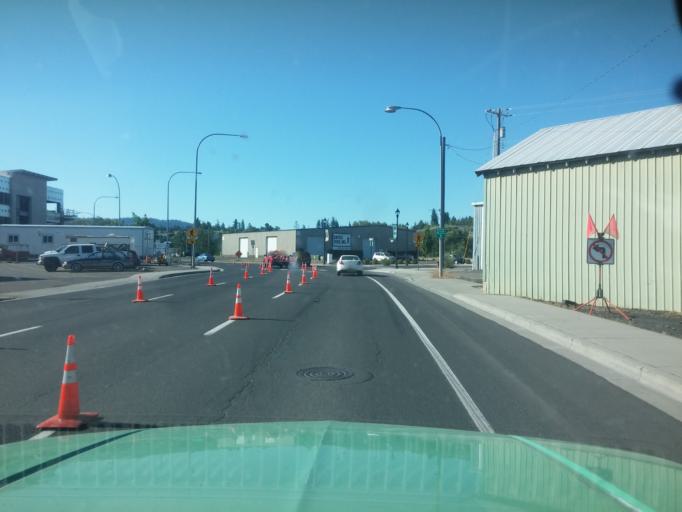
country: US
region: Idaho
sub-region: Latah County
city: Moscow
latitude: 46.7287
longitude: -117.0029
